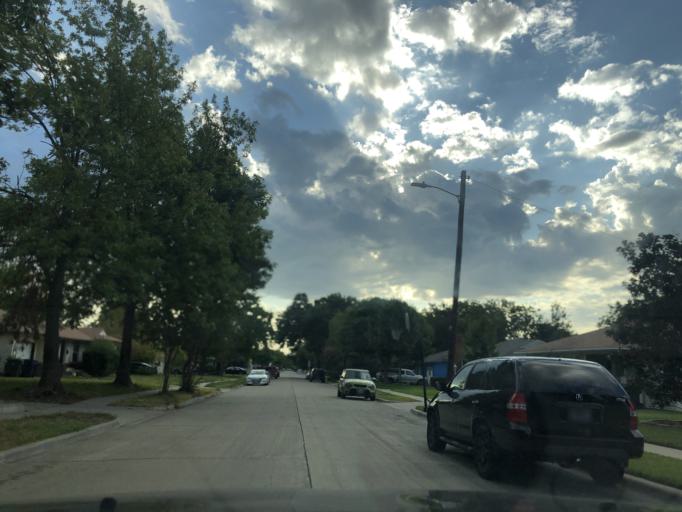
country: US
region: Texas
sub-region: Dallas County
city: Garland
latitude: 32.8754
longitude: -96.6498
